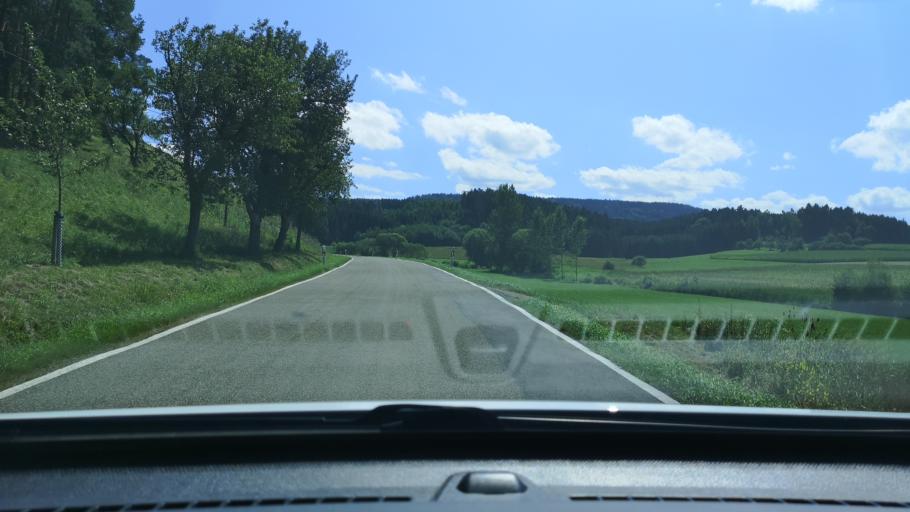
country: DE
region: Baden-Wuerttemberg
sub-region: Freiburg Region
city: Muhlheim am Bach
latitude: 48.3652
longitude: 8.7093
